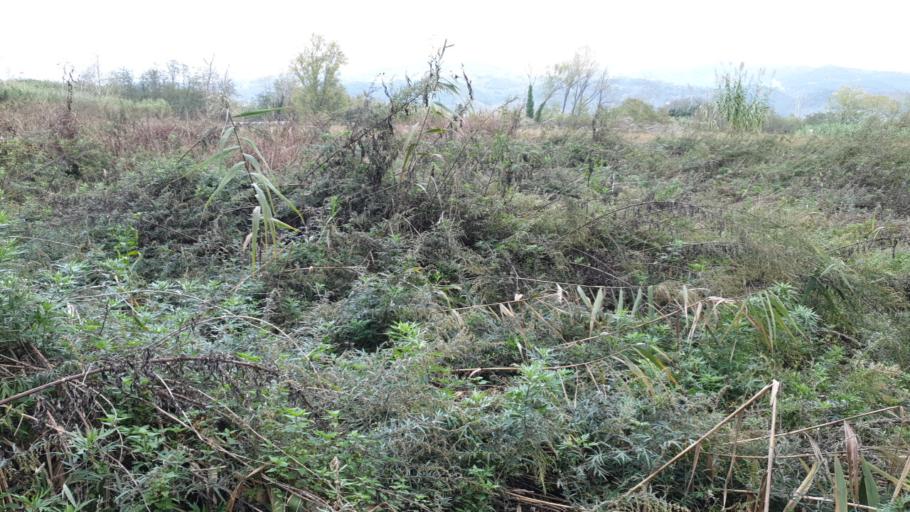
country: IT
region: Liguria
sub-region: Provincia di La Spezia
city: Arcola
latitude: 44.1330
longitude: 9.9162
